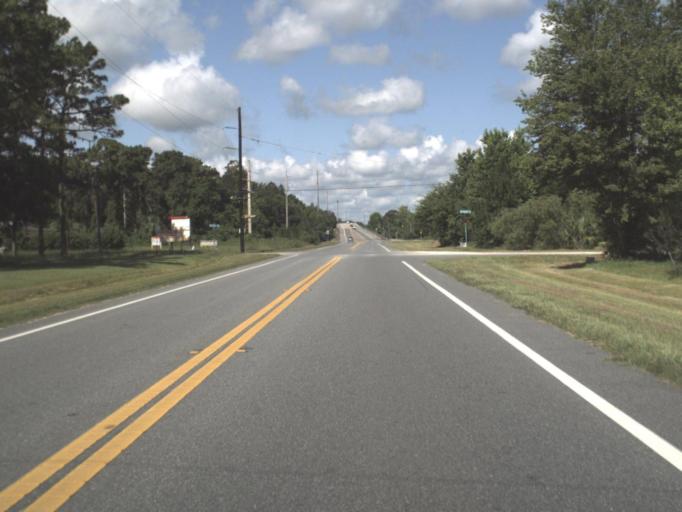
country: US
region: Florida
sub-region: Putnam County
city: Palatka
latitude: 29.5814
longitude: -81.6181
